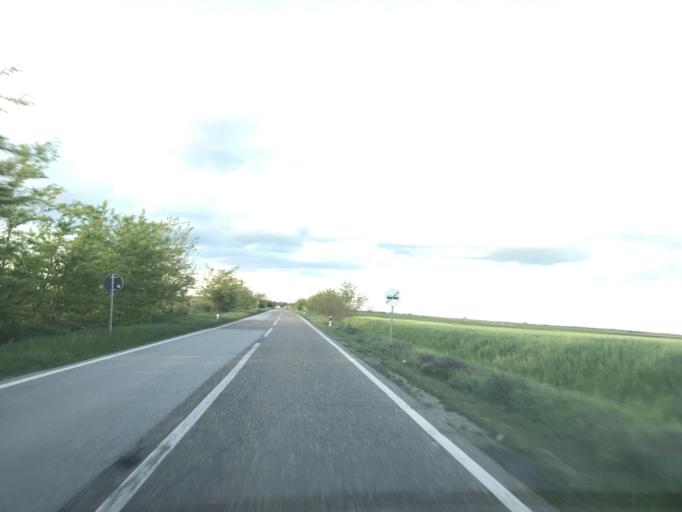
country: RS
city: Cestereg
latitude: 45.5493
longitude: 20.5147
